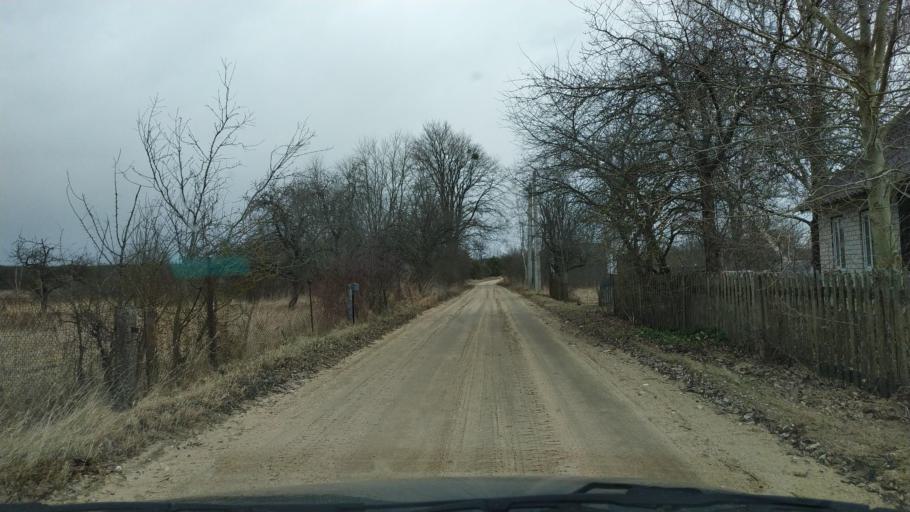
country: BY
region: Brest
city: Kamyanyets
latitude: 52.4124
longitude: 24.0203
